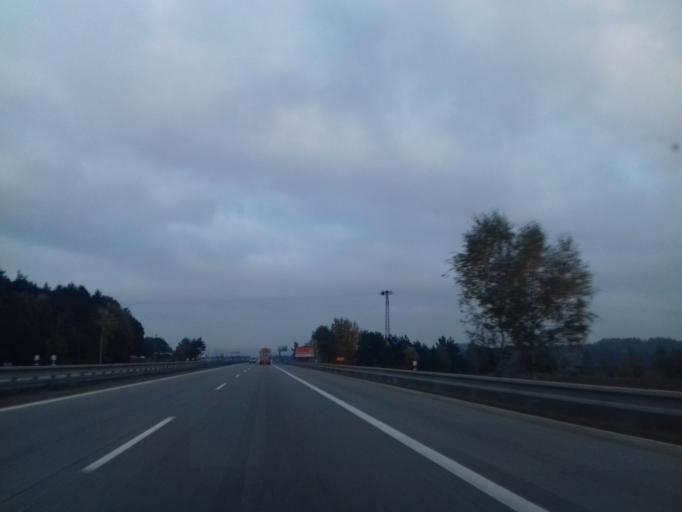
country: CZ
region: Central Bohemia
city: Cechtice
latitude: 49.6097
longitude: 15.1477
